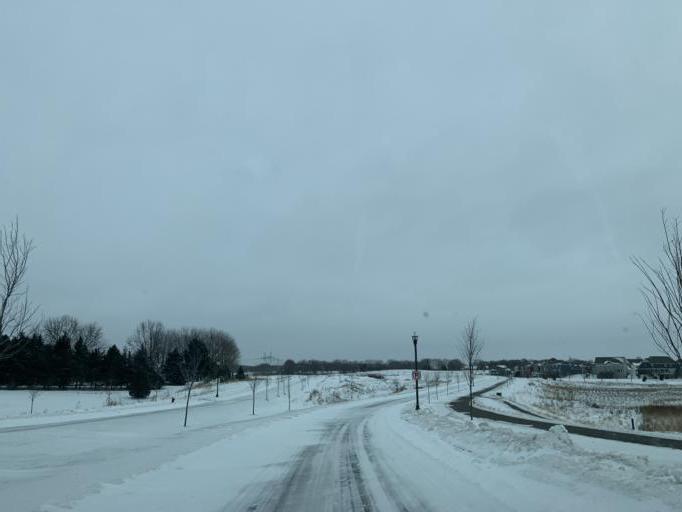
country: US
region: Minnesota
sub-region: Washington County
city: Cottage Grove
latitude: 44.8551
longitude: -92.9172
